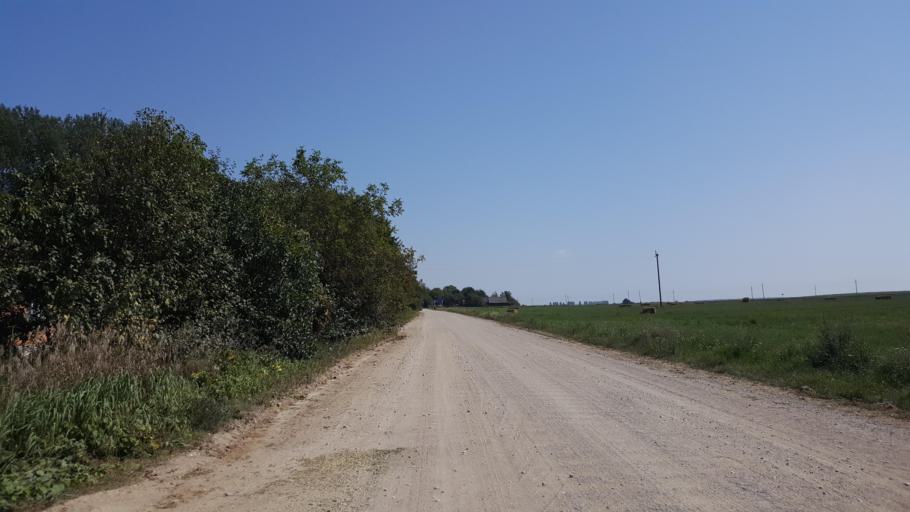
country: PL
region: Podlasie
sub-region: Powiat hajnowski
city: Czeremcha
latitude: 52.4684
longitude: 23.4755
